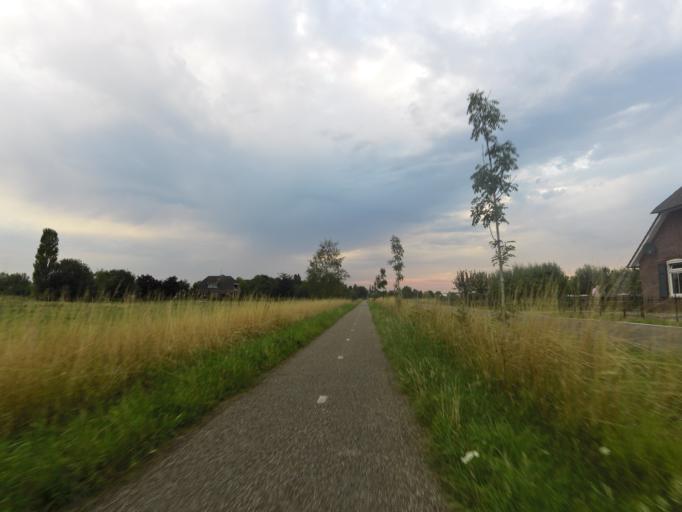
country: NL
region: Gelderland
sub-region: Oude IJsselstreek
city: Gendringen
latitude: 51.9121
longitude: 6.3487
